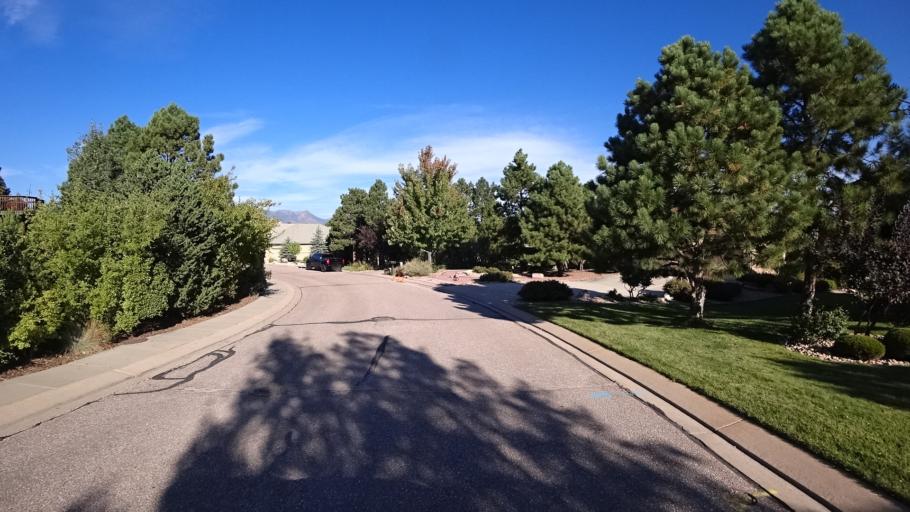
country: US
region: Colorado
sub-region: El Paso County
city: Colorado Springs
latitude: 38.9030
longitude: -104.7922
